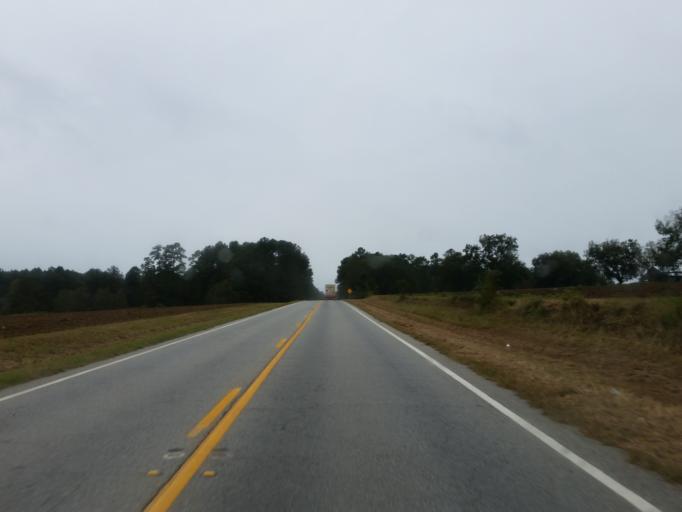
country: US
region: Georgia
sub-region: Berrien County
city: Ray City
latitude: 31.1071
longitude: -83.2872
